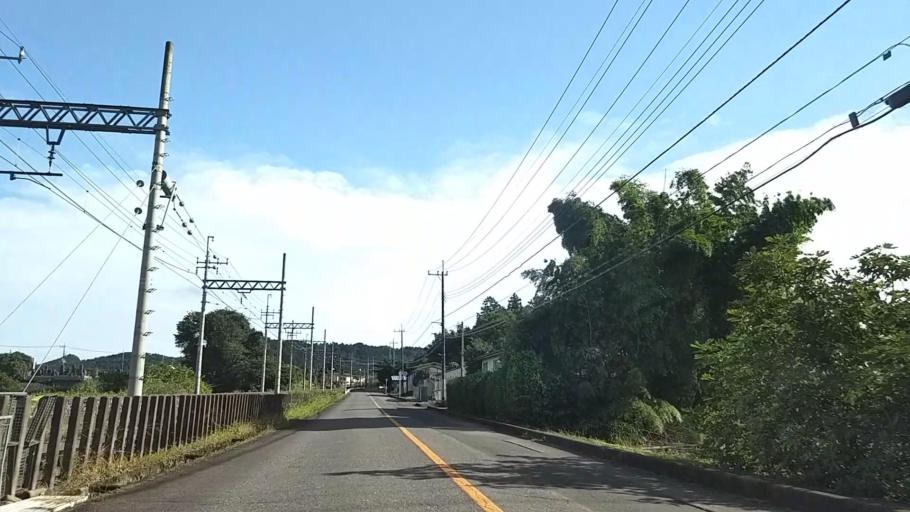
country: JP
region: Tochigi
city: Imaichi
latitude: 36.7657
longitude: 139.7153
